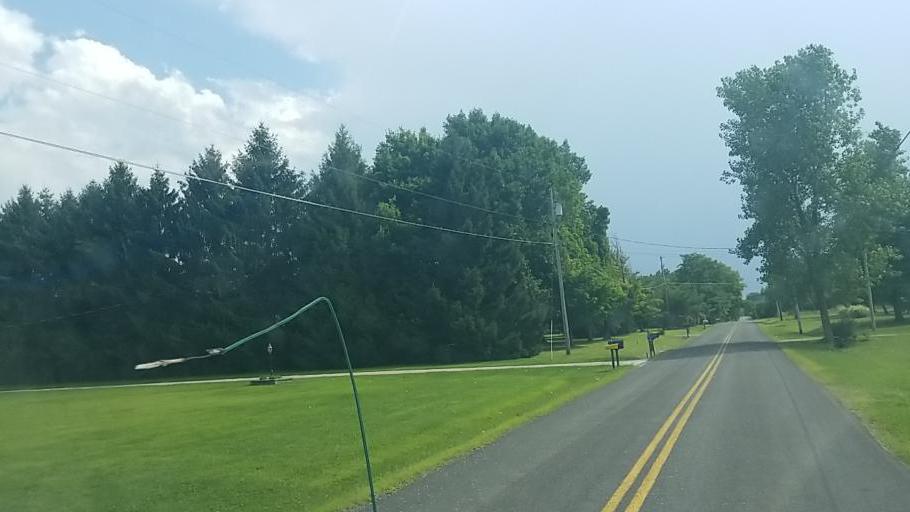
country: US
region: Ohio
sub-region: Medina County
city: Westfield Center
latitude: 41.1163
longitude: -81.9625
